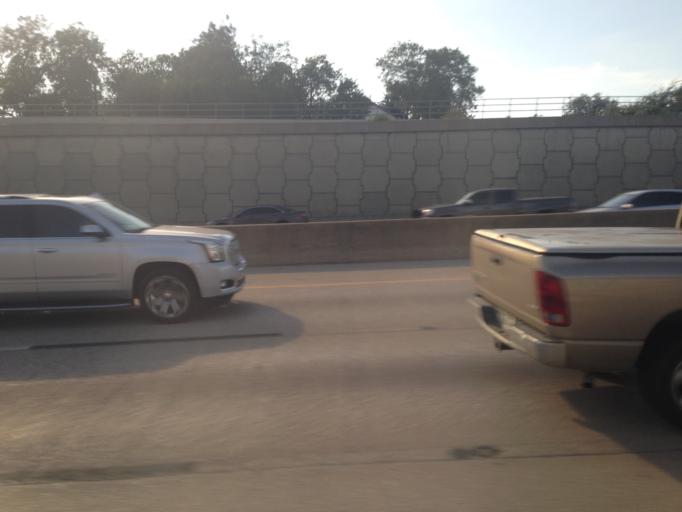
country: US
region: Texas
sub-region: Tarrant County
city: Fort Worth
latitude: 32.7134
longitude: -97.3204
